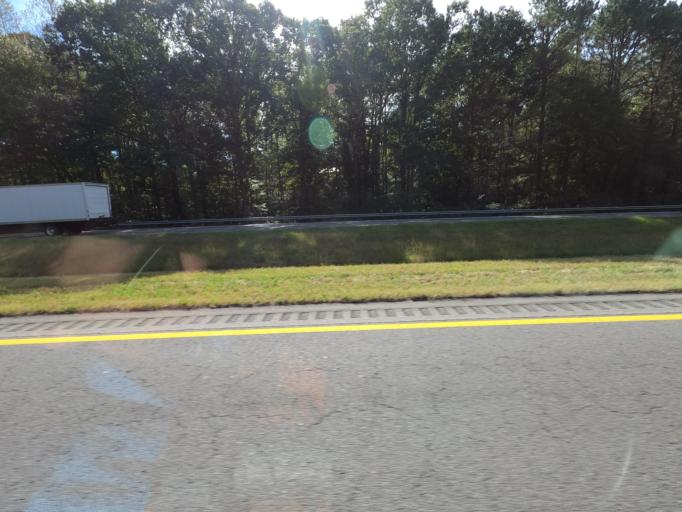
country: US
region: Tennessee
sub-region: Dickson County
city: Dickson
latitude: 35.9955
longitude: -87.4719
